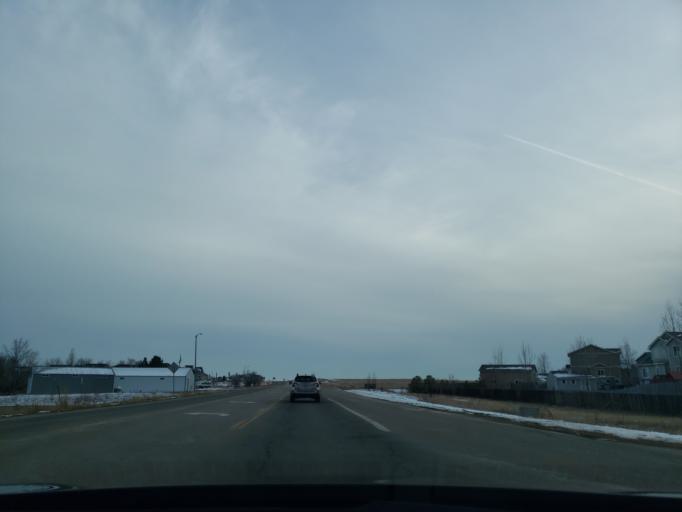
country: US
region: Colorado
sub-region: Larimer County
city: Campion
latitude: 40.3441
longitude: -105.0937
